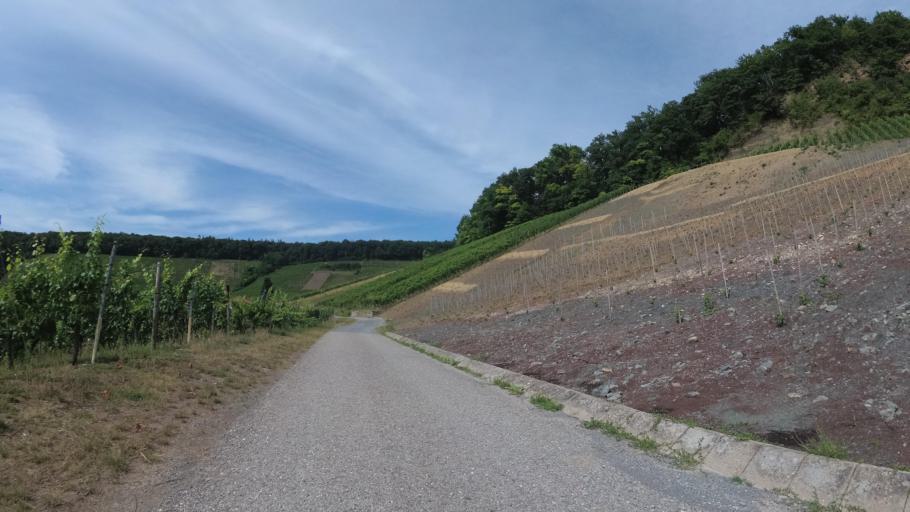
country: DE
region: Baden-Wuerttemberg
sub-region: Regierungsbezirk Stuttgart
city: Eberstadt
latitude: 49.1913
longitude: 9.3132
